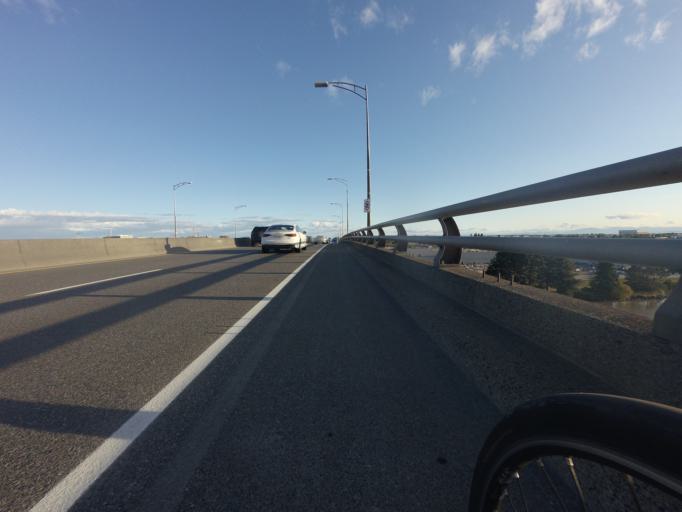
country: CA
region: British Columbia
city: Richmond
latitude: 49.1992
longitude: -123.1363
